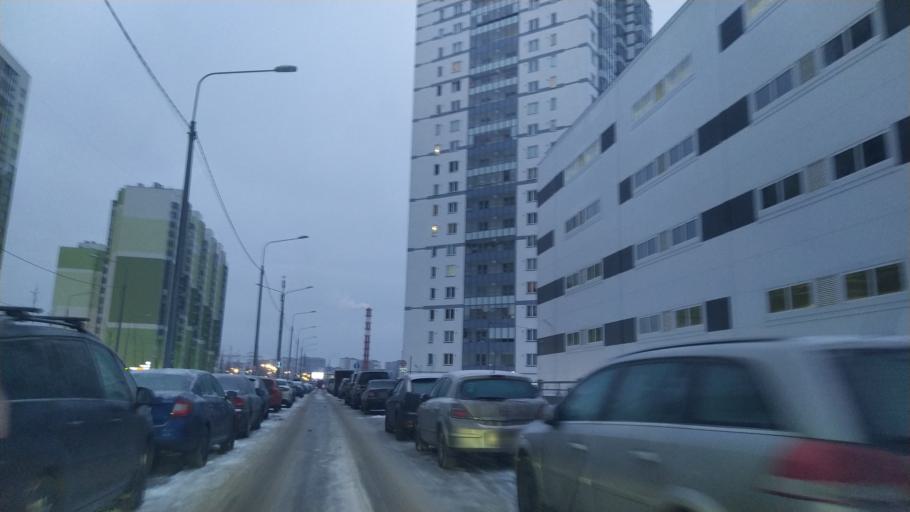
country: RU
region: Leningrad
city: Murino
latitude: 60.0354
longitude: 30.4532
